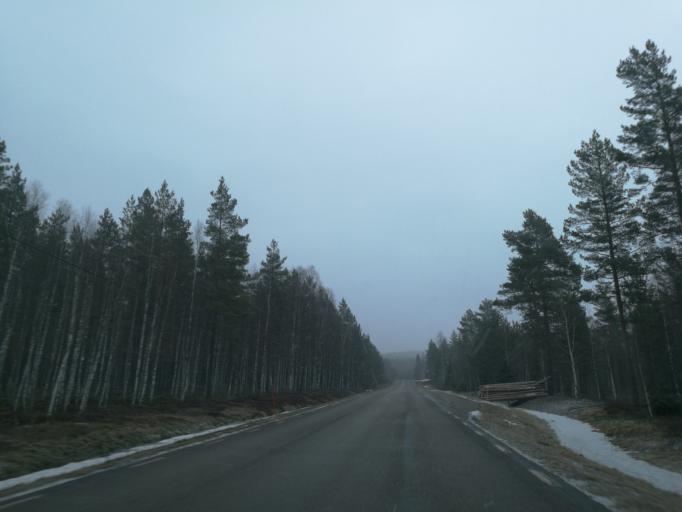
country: NO
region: Hedmark
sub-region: Asnes
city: Flisa
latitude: 60.6976
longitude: 12.5112
